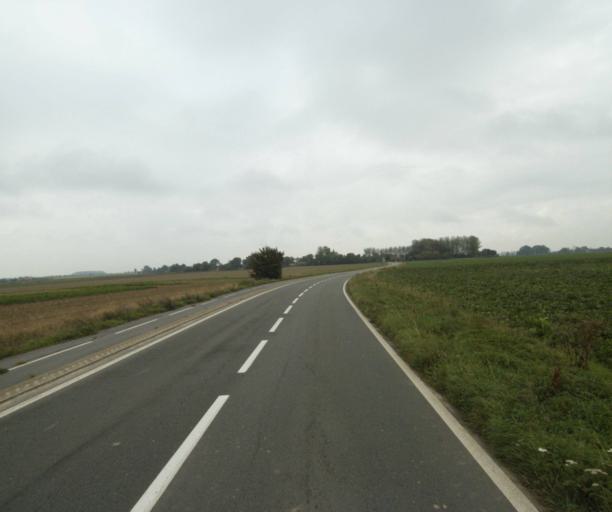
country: FR
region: Nord-Pas-de-Calais
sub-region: Departement du Nord
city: Radinghem-en-Weppes
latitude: 50.5999
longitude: 2.9069
